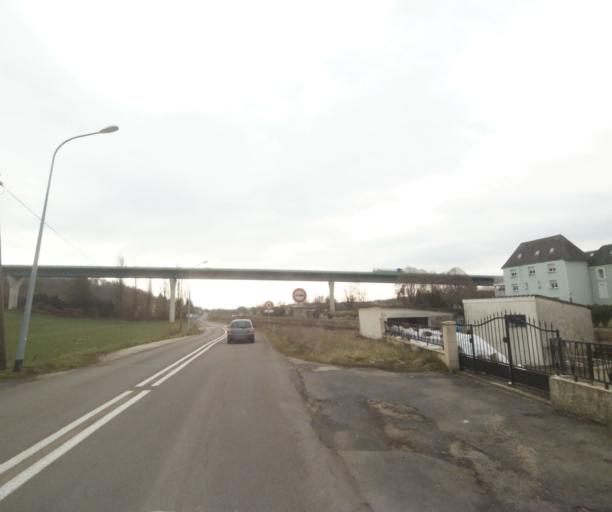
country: FR
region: Lorraine
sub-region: Departement de la Meuse
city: Ancerville
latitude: 48.6279
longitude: 4.9935
